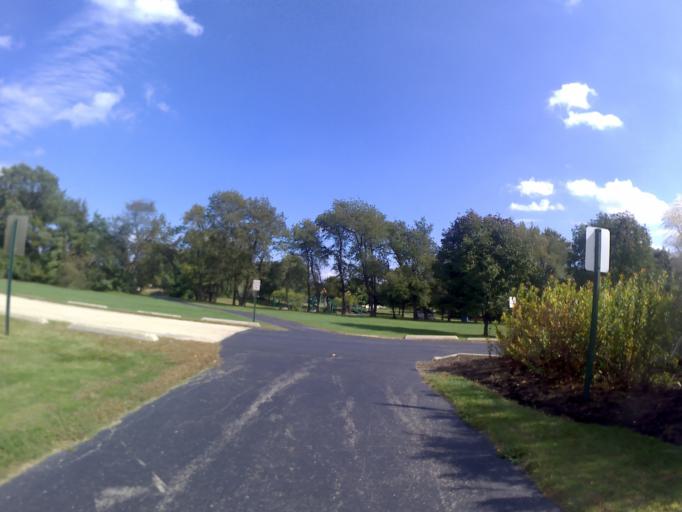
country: US
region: Illinois
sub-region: Will County
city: Bolingbrook
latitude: 41.7104
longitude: -88.1128
